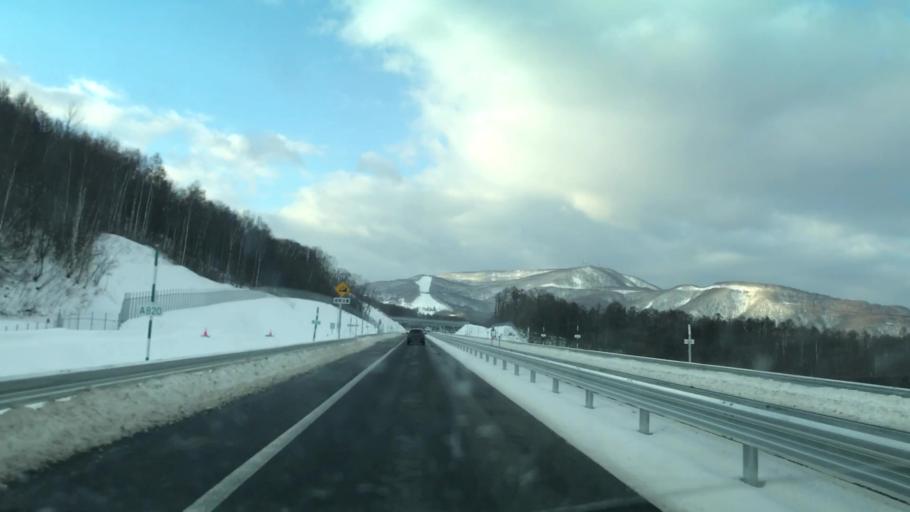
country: JP
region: Hokkaido
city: Otaru
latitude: 43.1675
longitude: 141.0640
